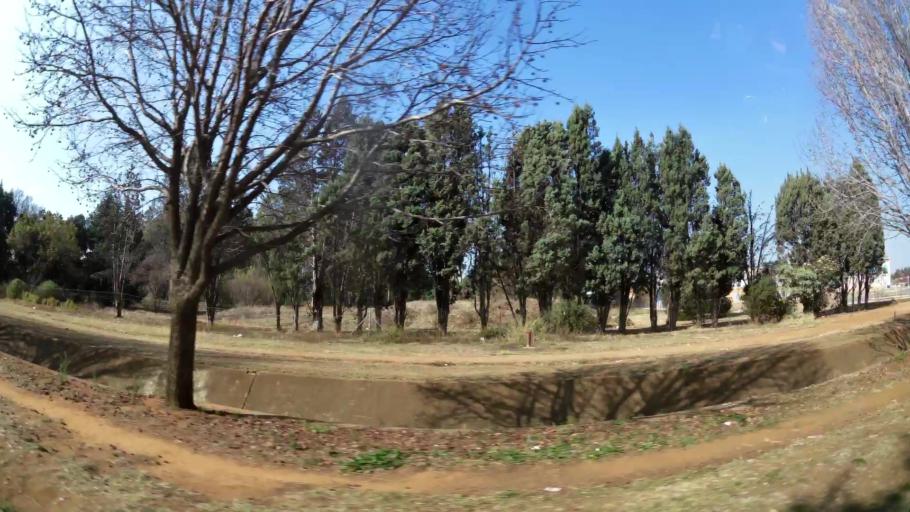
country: ZA
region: Gauteng
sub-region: West Rand District Municipality
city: Randfontein
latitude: -26.1710
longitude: 27.6894
